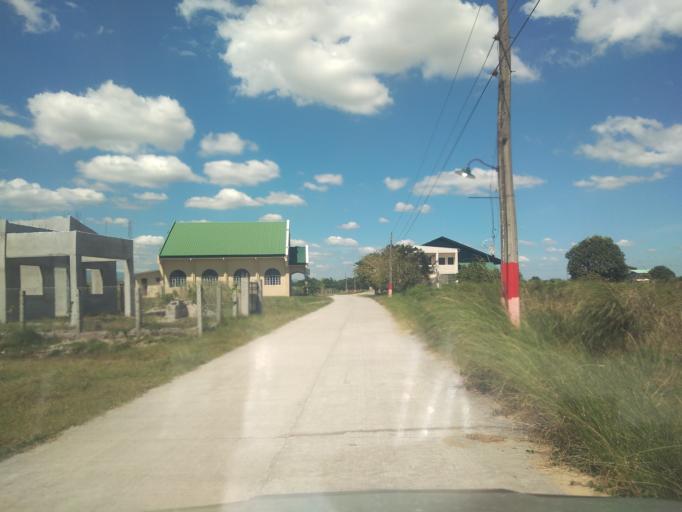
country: PH
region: Central Luzon
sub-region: Province of Pampanga
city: San Basilio
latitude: 15.0344
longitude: 120.6052
